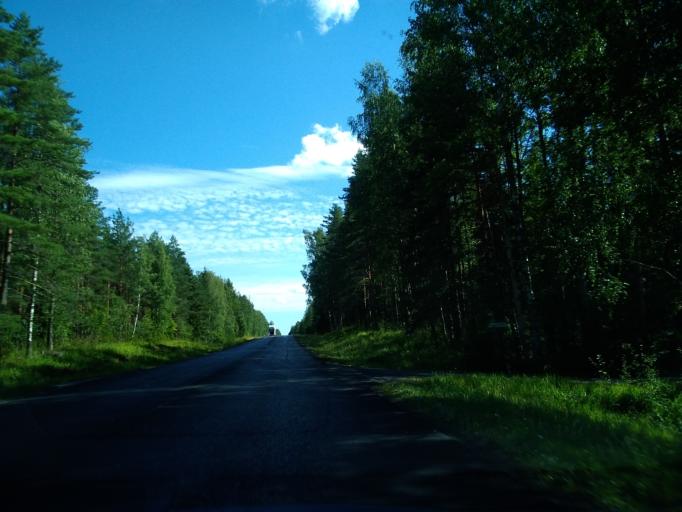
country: FI
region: Haeme
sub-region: Haemeenlinna
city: Renko
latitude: 60.9313
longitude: 24.3596
